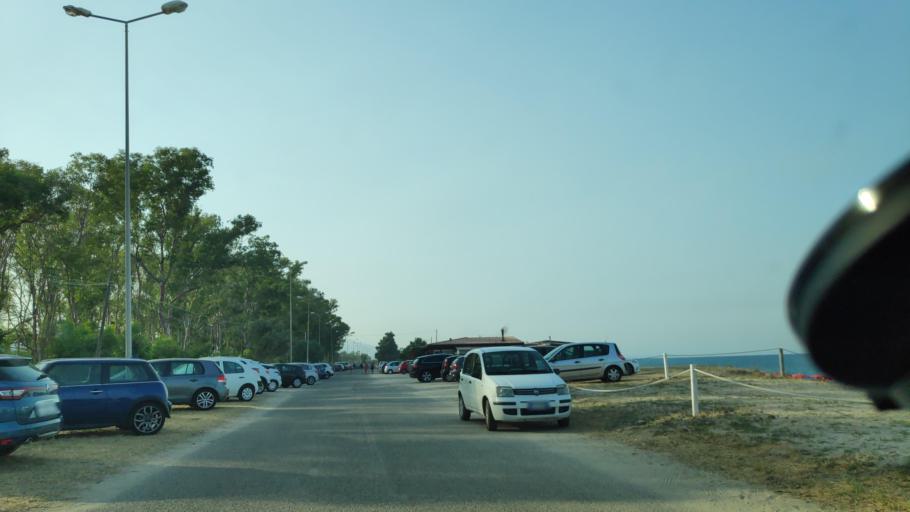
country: IT
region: Calabria
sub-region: Provincia di Catanzaro
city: Isca Marina
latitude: 38.6136
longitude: 16.5617
